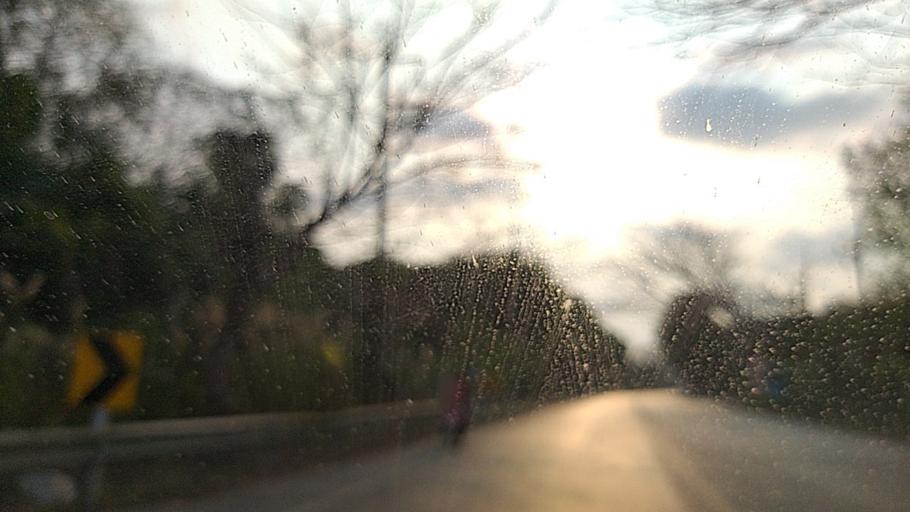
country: TH
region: Trat
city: Khao Saming
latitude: 12.2899
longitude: 102.3288
